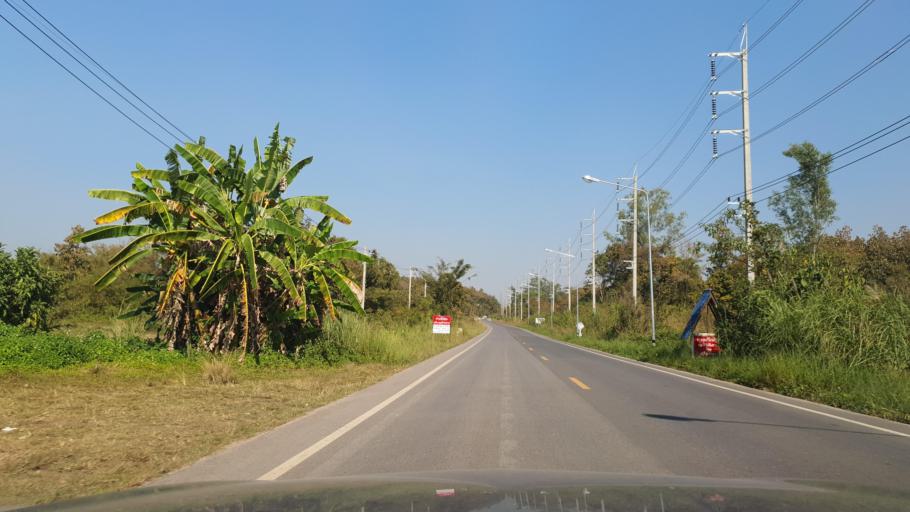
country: TH
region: Chiang Rai
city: Mae Lao
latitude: 19.8183
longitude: 99.6845
